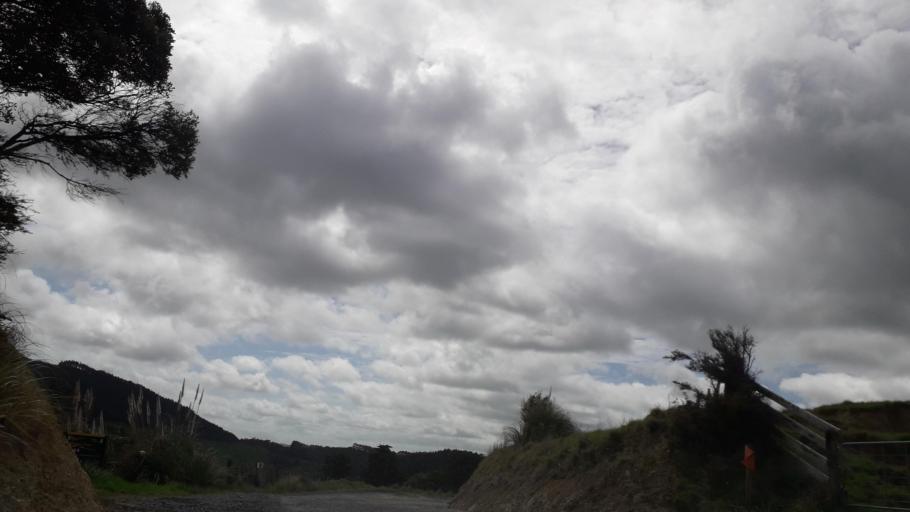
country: NZ
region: Northland
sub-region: Far North District
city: Kaitaia
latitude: -35.1921
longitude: 173.2876
